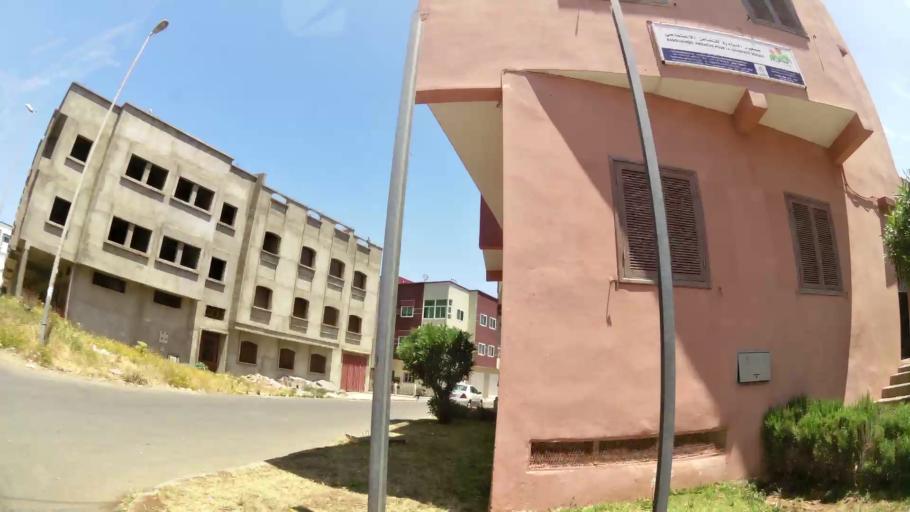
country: MA
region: Gharb-Chrarda-Beni Hssen
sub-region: Kenitra Province
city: Kenitra
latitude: 34.2541
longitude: -6.6208
